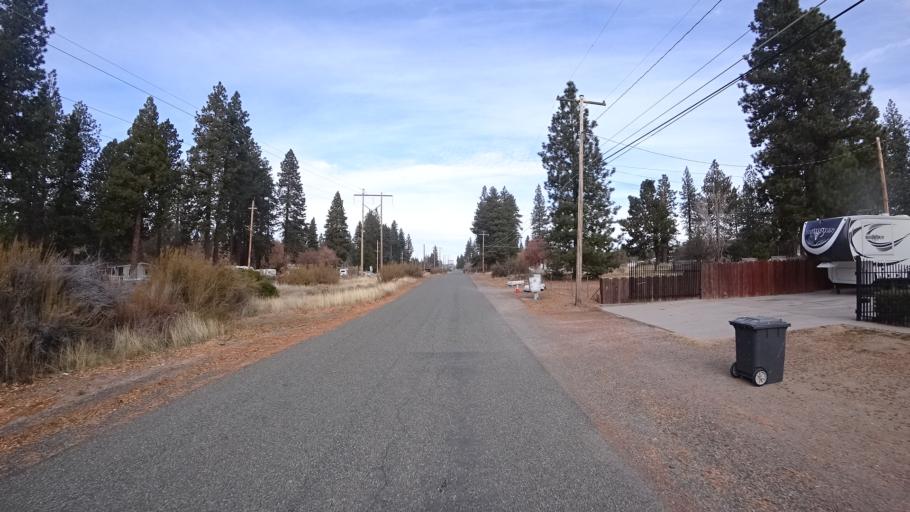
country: US
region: California
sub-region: Siskiyou County
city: Weed
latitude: 41.4470
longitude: -122.3619
